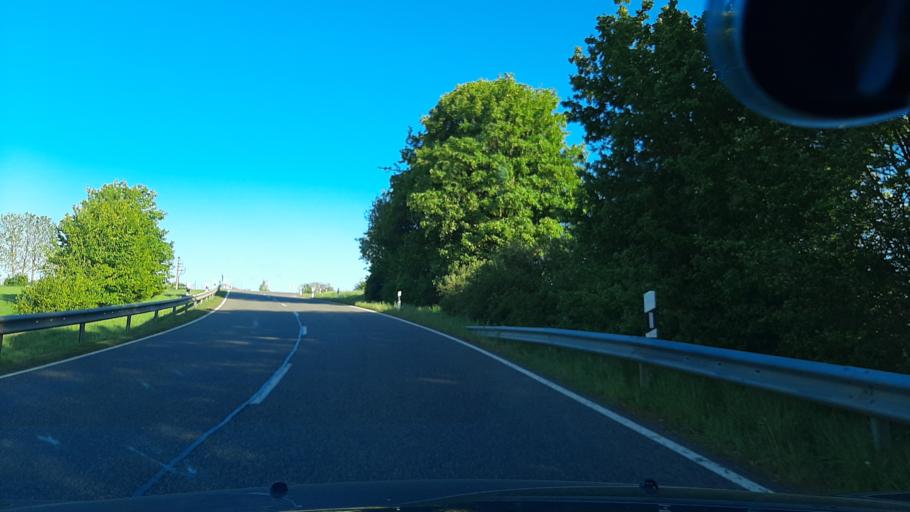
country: DE
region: Rheinland-Pfalz
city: Ohlenhard
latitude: 50.4777
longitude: 6.7113
